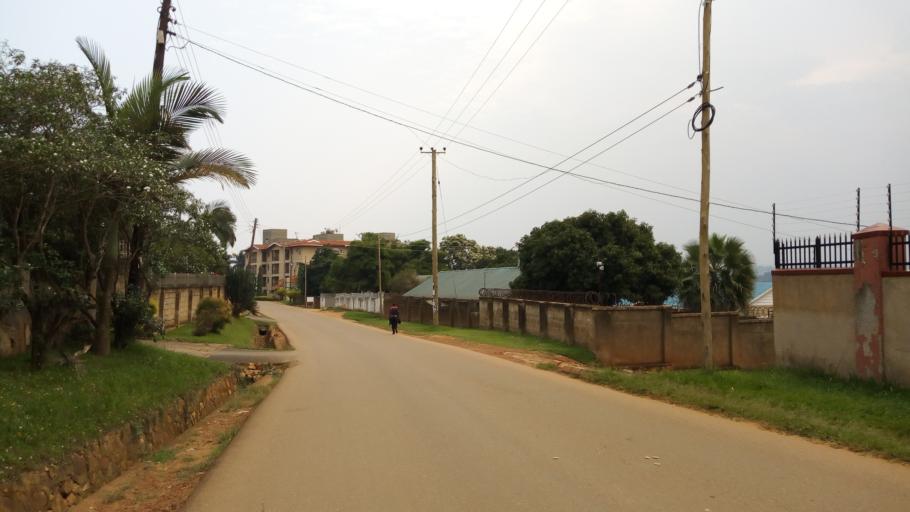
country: UG
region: Central Region
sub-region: Wakiso District
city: Kireka
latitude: 0.3176
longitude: 32.6404
